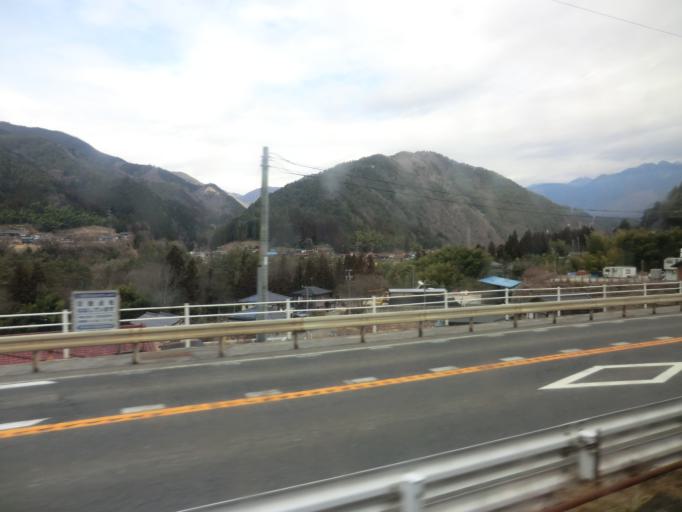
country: JP
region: Nagano
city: Iida
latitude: 35.6842
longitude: 137.6620
